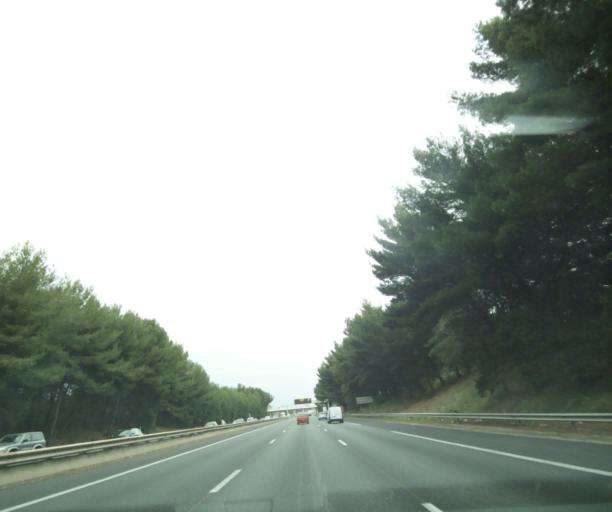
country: FR
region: Languedoc-Roussillon
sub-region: Departement de l'Herault
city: Lattes
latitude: 43.5989
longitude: 3.9159
